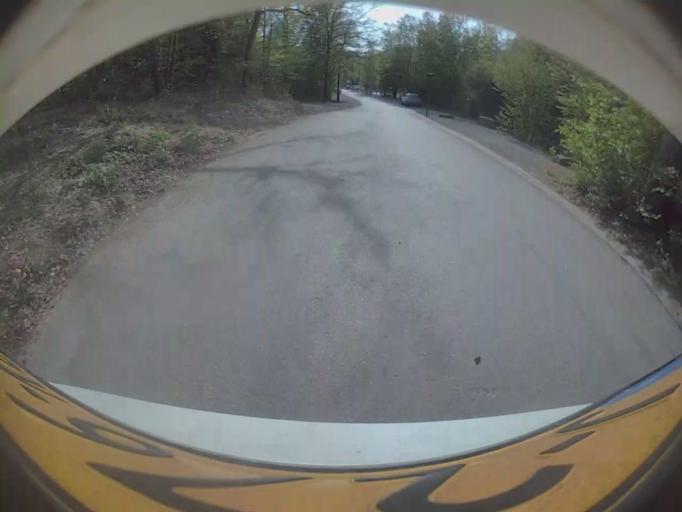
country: BE
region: Wallonia
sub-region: Province du Luxembourg
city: Durbuy
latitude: 50.3451
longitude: 5.4266
